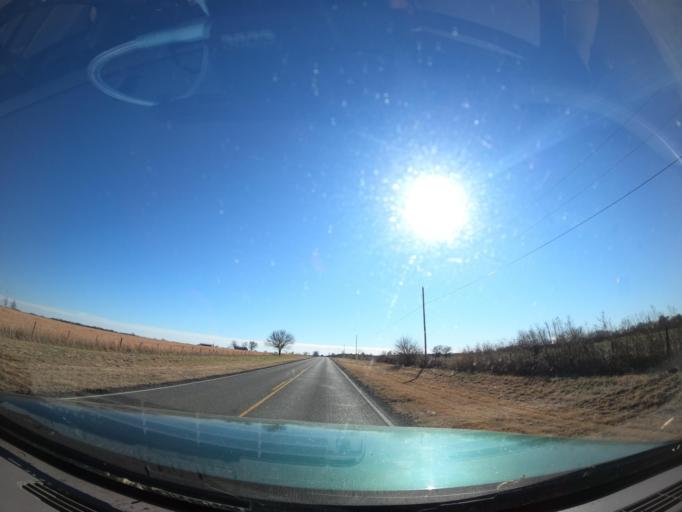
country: US
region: Oklahoma
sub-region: Muskogee County
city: Haskell
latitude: 35.6881
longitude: -95.6423
